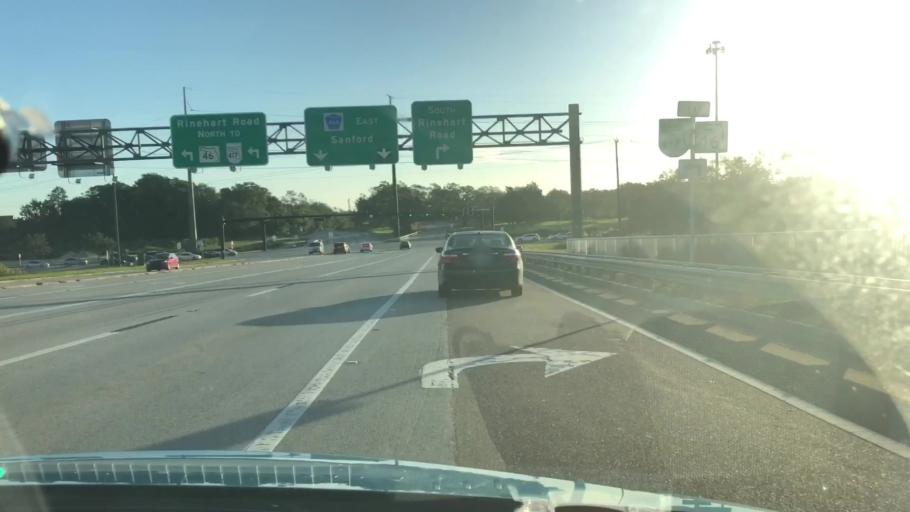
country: US
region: Florida
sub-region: Seminole County
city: Heathrow
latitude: 28.7863
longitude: -81.3490
